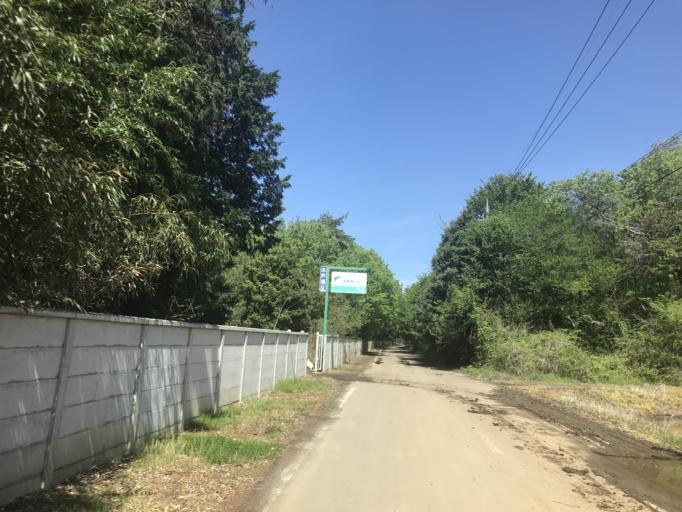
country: JP
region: Ibaraki
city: Shimodate
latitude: 36.2858
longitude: 140.0203
